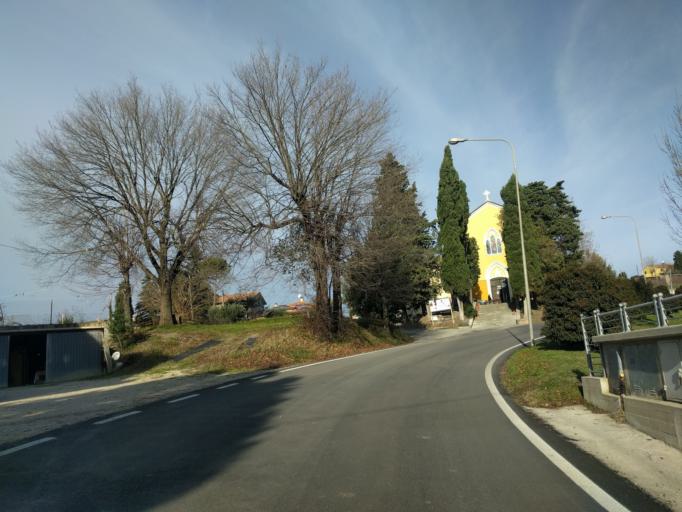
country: IT
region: The Marches
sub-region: Provincia di Pesaro e Urbino
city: Cuccurano
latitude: 43.7964
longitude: 12.9512
